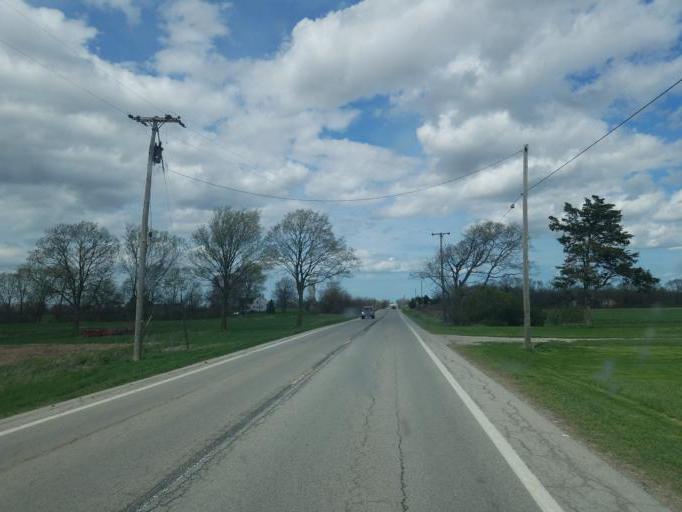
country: US
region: Ohio
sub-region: Huron County
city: Bellevue
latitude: 41.3285
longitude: -82.7650
